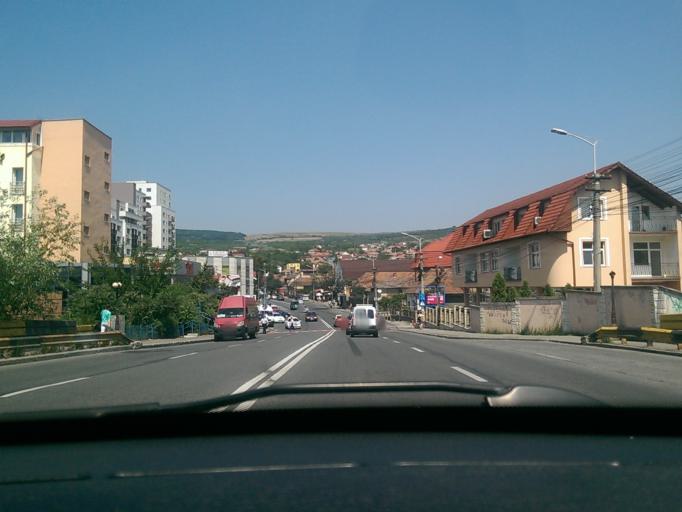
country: RO
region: Cluj
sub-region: Municipiul Cluj-Napoca
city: Cluj-Napoca
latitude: 46.7855
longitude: 23.5818
